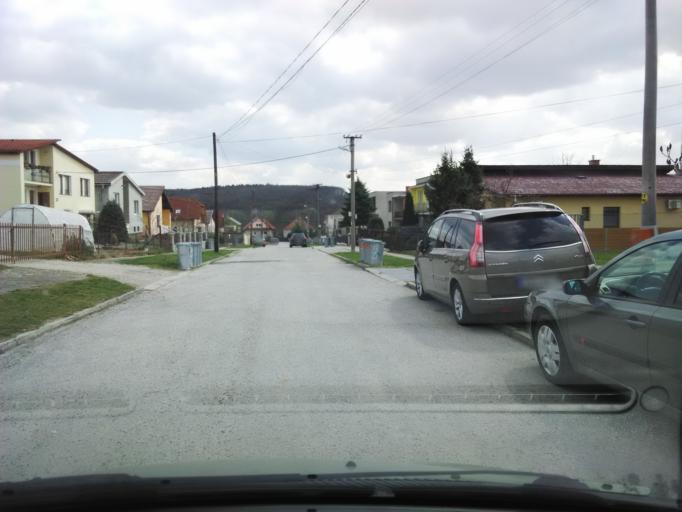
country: SK
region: Nitriansky
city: Zlate Moravce
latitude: 48.4189
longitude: 18.3597
